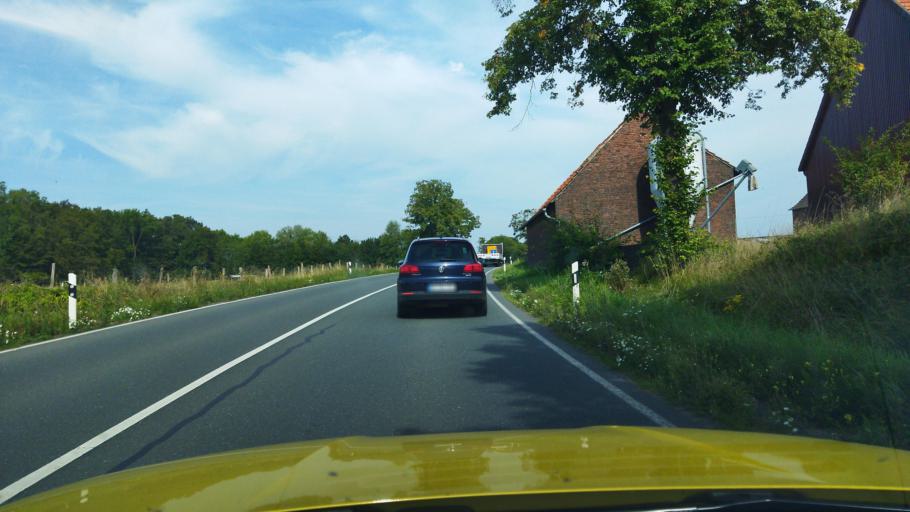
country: DE
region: North Rhine-Westphalia
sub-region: Regierungsbezirk Munster
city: Ennigerloh
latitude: 51.8738
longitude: 8.0339
